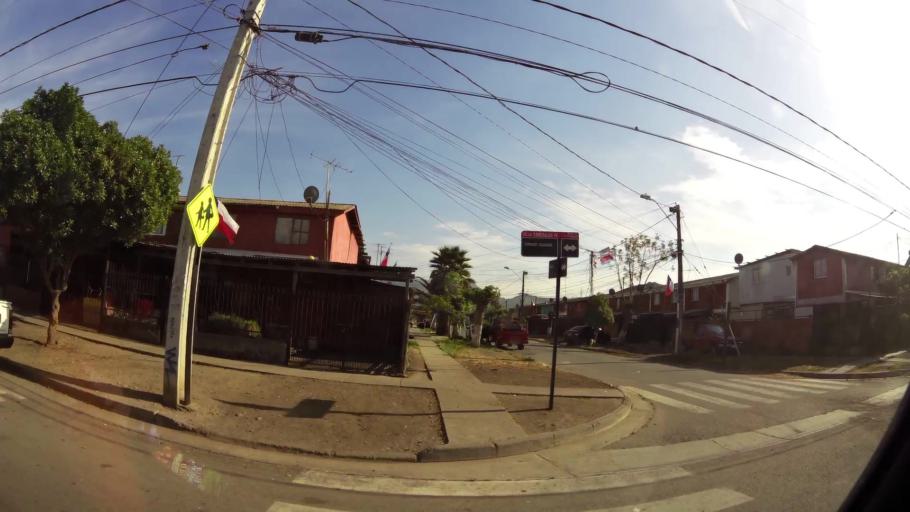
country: CL
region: Santiago Metropolitan
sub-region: Provincia de Talagante
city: Talagante
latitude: -33.6750
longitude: -70.9426
